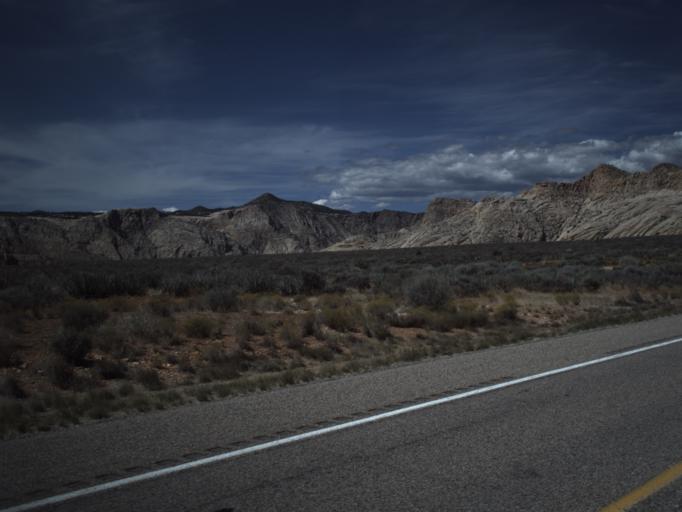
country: US
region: Utah
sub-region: Washington County
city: Ivins
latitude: 37.2178
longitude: -113.6332
